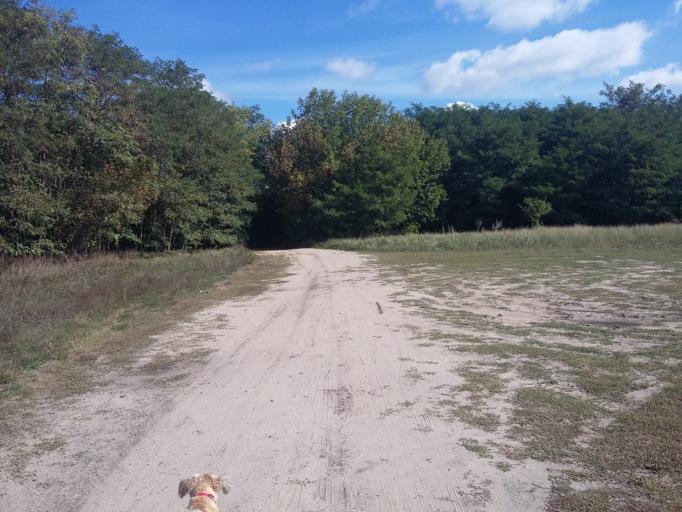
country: PL
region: Lodz Voivodeship
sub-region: Powiat pabianicki
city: Ksawerow
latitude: 51.7239
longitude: 19.3956
